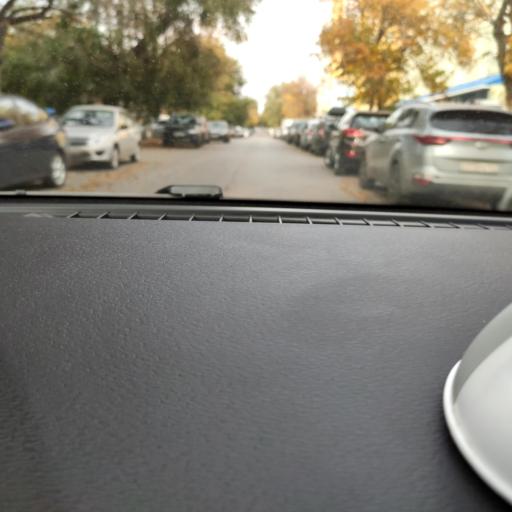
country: RU
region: Samara
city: Samara
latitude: 53.1823
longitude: 50.1032
